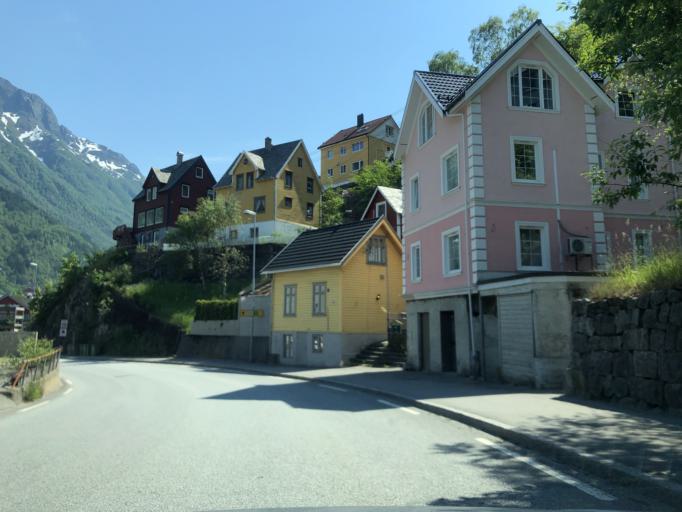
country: NO
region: Hordaland
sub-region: Odda
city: Odda
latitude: 60.0715
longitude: 6.5394
